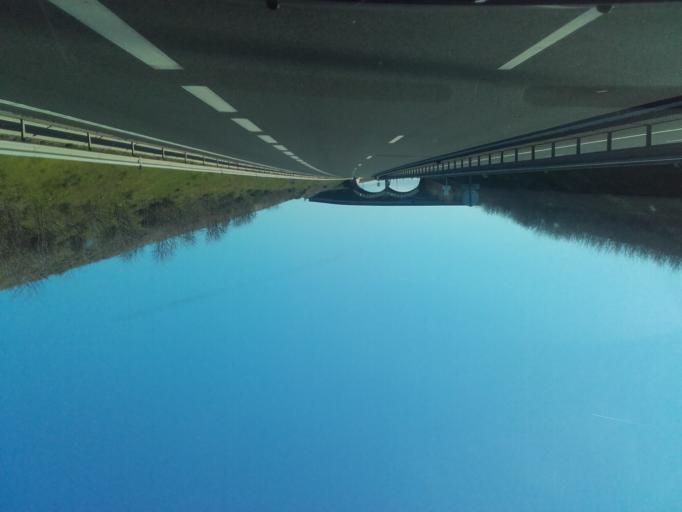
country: FR
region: Rhone-Alpes
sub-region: Departement de l'Ain
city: Beynost
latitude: 45.8495
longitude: 5.0097
